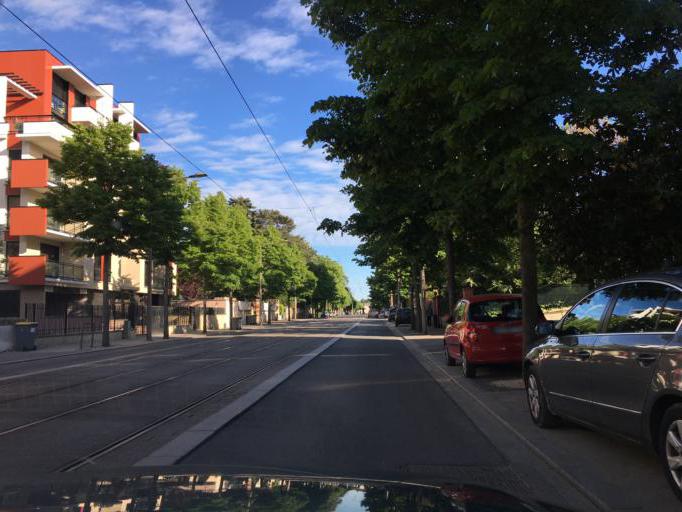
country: FR
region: Centre
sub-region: Departement du Loiret
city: Saint-Jean-le-Blanc
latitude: 47.8859
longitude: 1.9075
